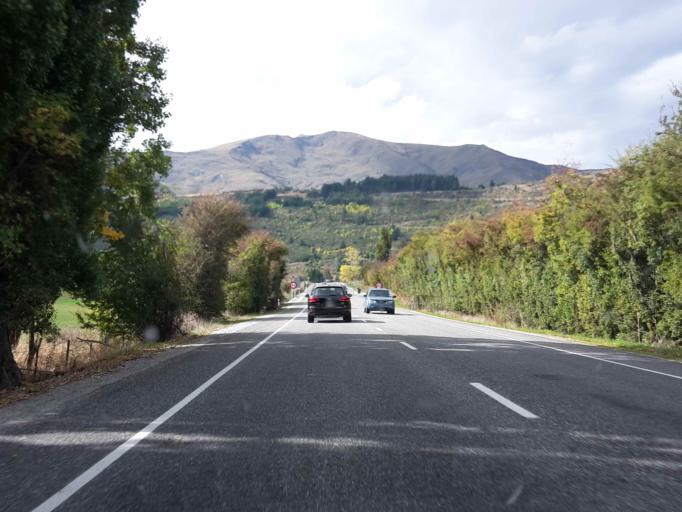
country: NZ
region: Otago
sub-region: Queenstown-Lakes District
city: Arrowtown
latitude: -44.9802
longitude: 168.8429
